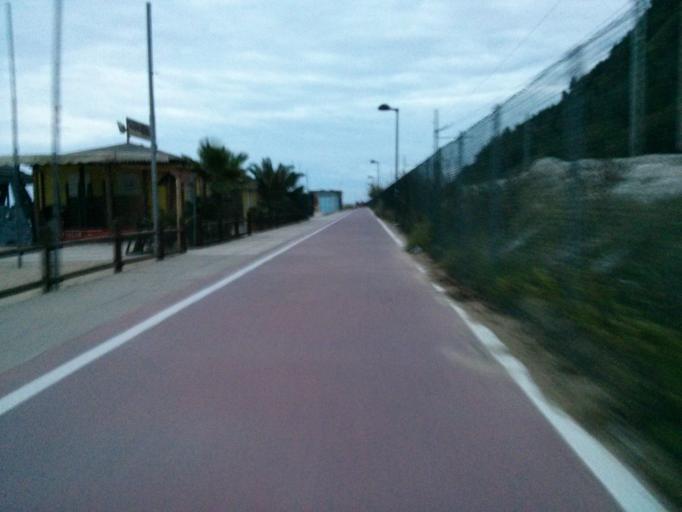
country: IT
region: The Marches
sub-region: Provincia di Pesaro e Urbino
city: Pesaro
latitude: 43.9004
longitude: 12.9371
